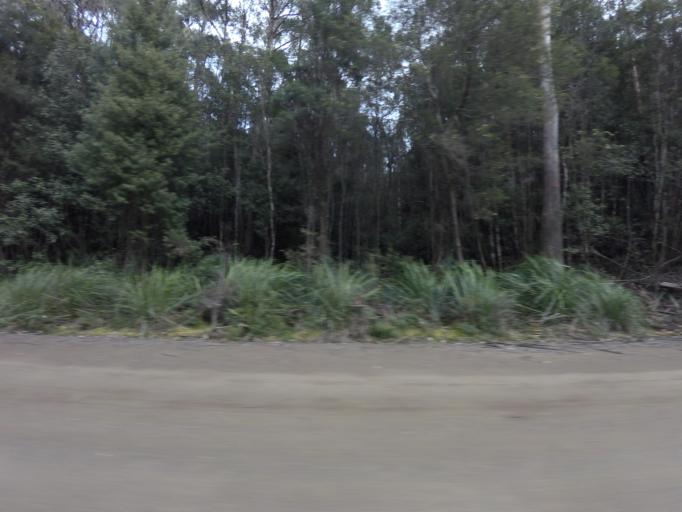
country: AU
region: Tasmania
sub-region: Huon Valley
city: Geeveston
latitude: -43.5222
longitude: 146.8818
